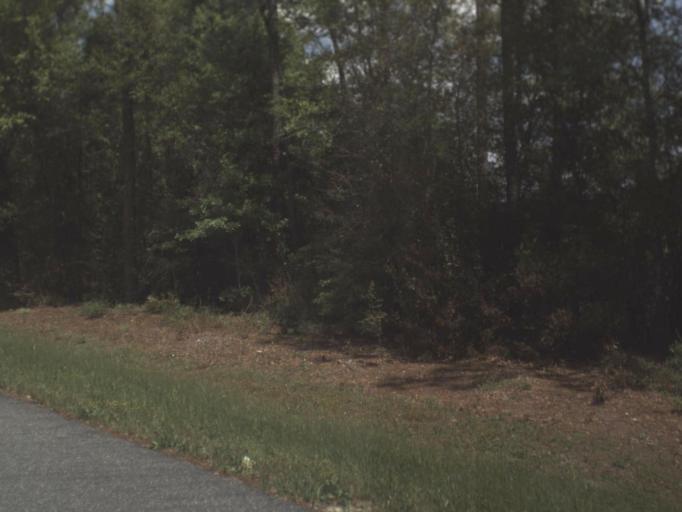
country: US
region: Florida
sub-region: Santa Rosa County
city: Point Baker
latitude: 30.7200
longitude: -87.0450
